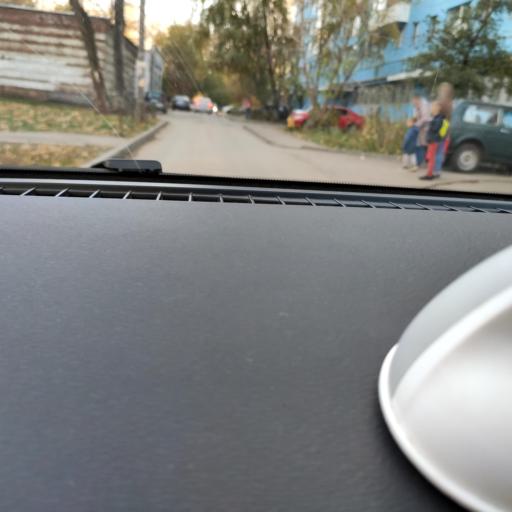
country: RU
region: Samara
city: Samara
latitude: 53.2404
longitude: 50.2146
